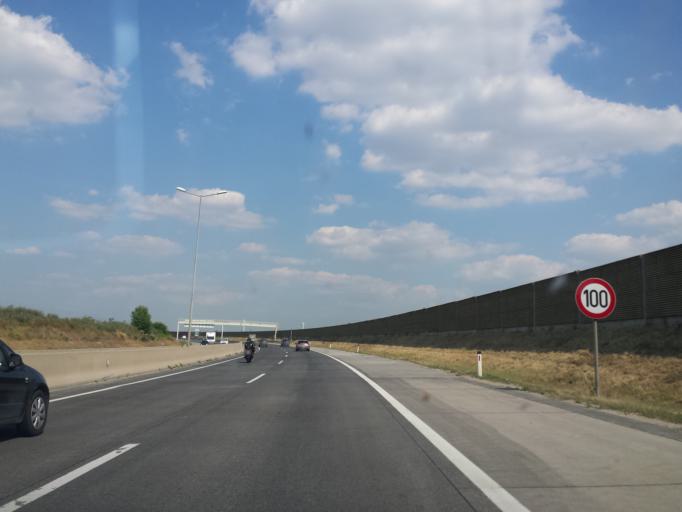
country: AT
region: Lower Austria
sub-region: Politischer Bezirk Wien-Umgebung
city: Gerasdorf bei Wien
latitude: 48.2670
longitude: 16.4918
